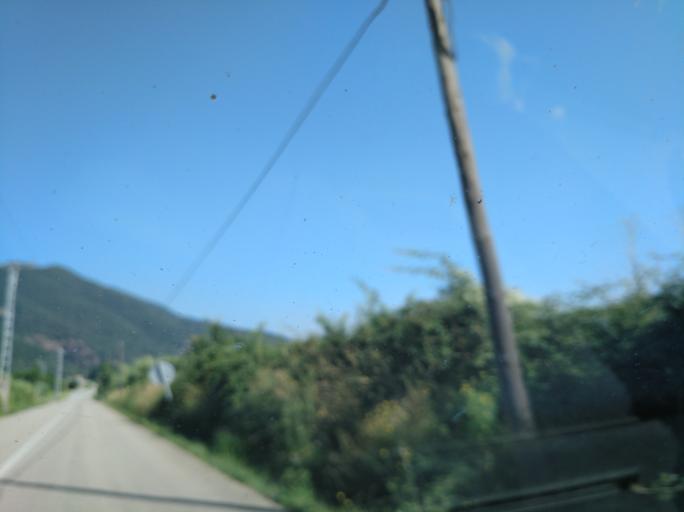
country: ES
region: Catalonia
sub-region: Provincia de Girona
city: la Cellera de Ter
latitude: 41.9768
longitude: 2.6160
